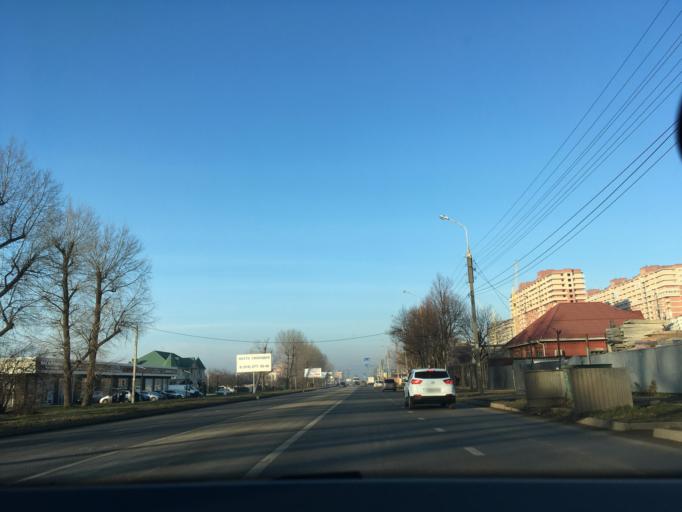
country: RU
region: Krasnodarskiy
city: Krasnodar
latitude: 45.1021
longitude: 39.0131
